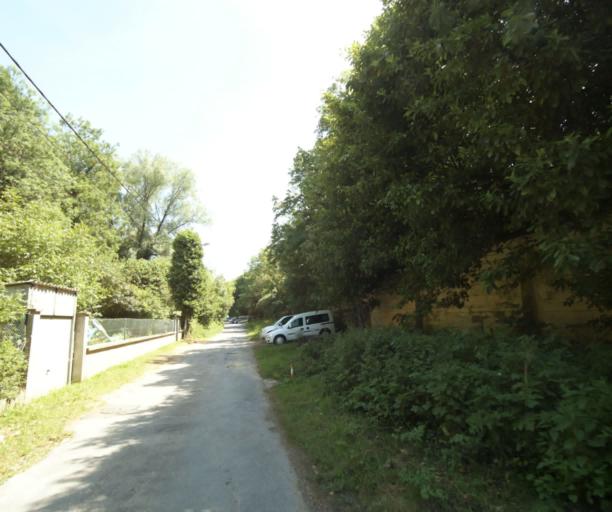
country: FR
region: Champagne-Ardenne
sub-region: Departement des Ardennes
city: Charleville-Mezieres
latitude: 49.7717
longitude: 4.7039
